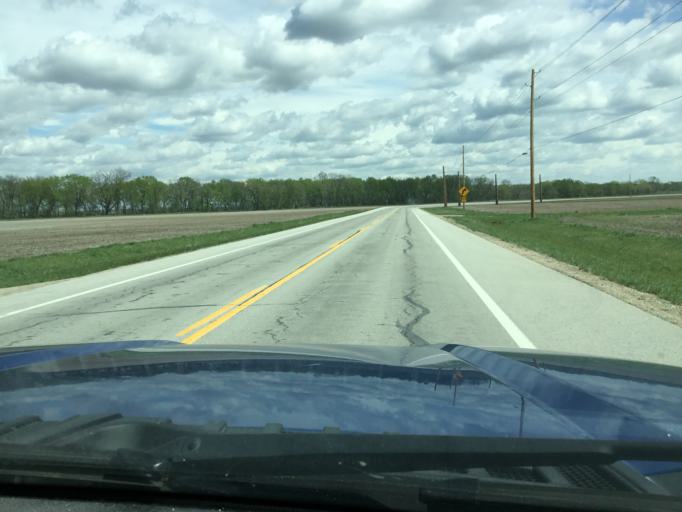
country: US
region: Kansas
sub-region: Douglas County
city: Lawrence
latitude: 38.9136
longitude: -95.2707
